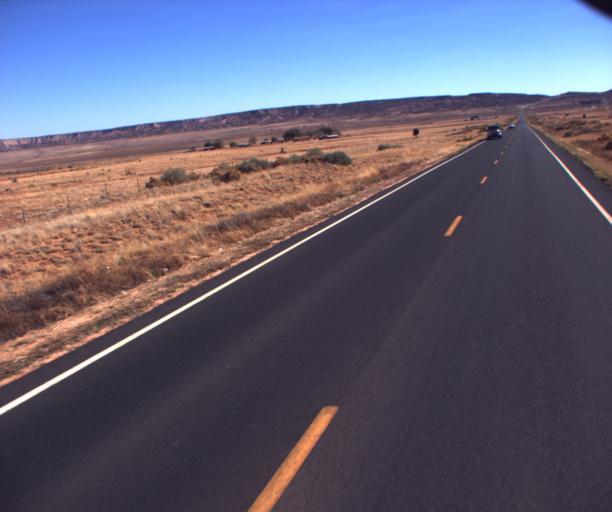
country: US
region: Arizona
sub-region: Apache County
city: Ganado
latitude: 35.7751
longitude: -109.6531
